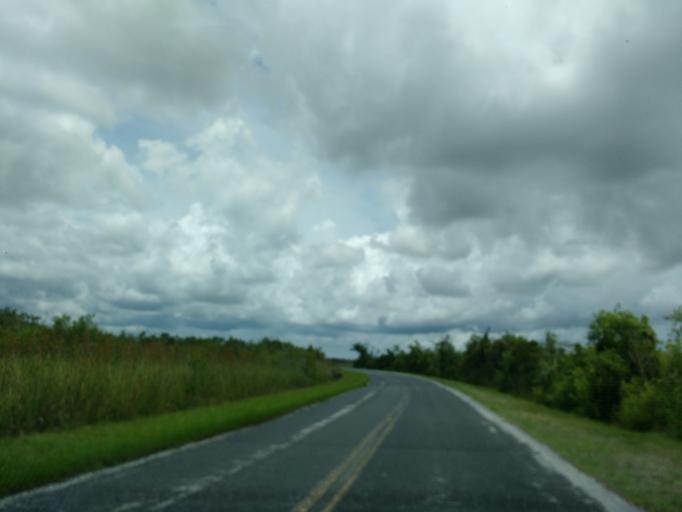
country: US
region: Florida
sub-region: Miami-Dade County
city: Florida City
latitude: 25.3856
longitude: -80.6110
